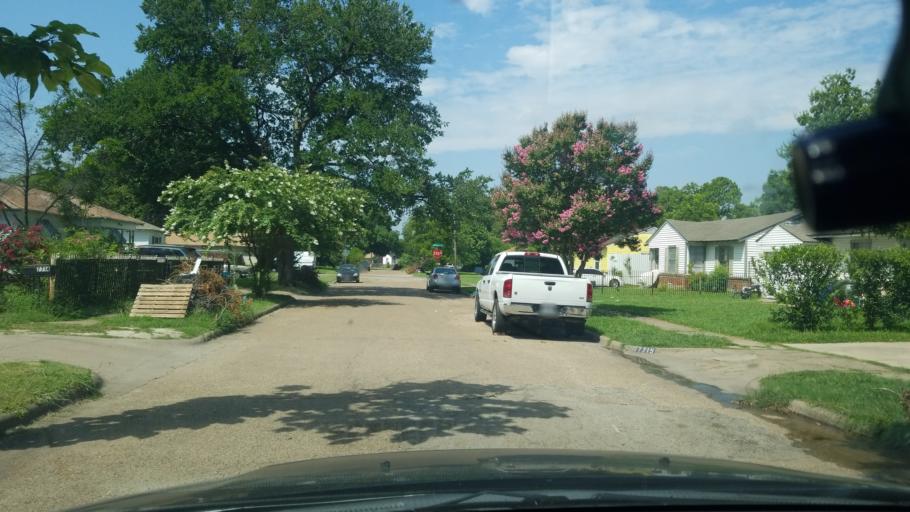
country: US
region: Texas
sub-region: Dallas County
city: Balch Springs
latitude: 32.7400
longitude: -96.6900
